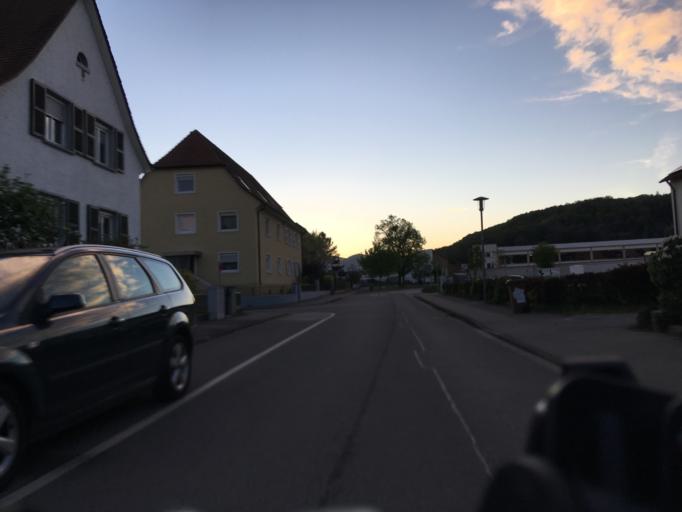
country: DE
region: Baden-Wuerttemberg
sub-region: Freiburg Region
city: Gottmadingen
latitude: 47.7352
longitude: 8.7843
